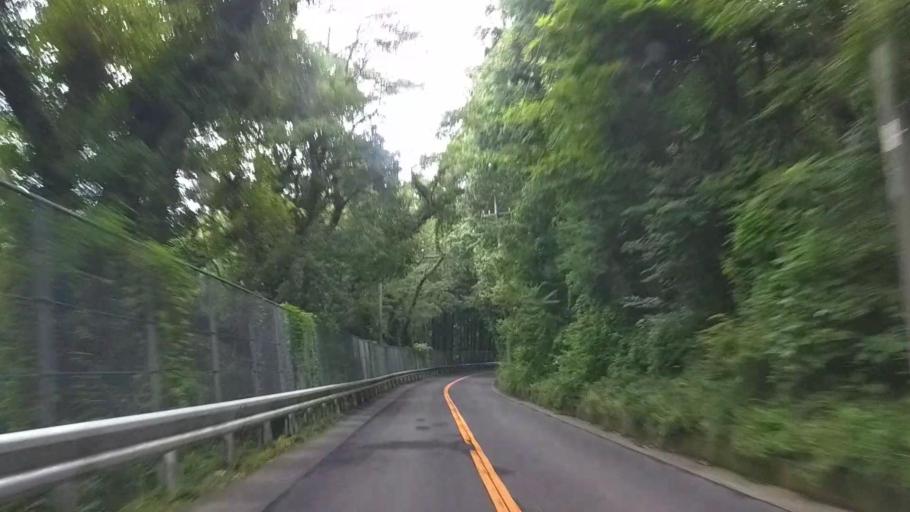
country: JP
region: Kanagawa
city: Ninomiya
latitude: 35.3362
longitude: 139.2370
